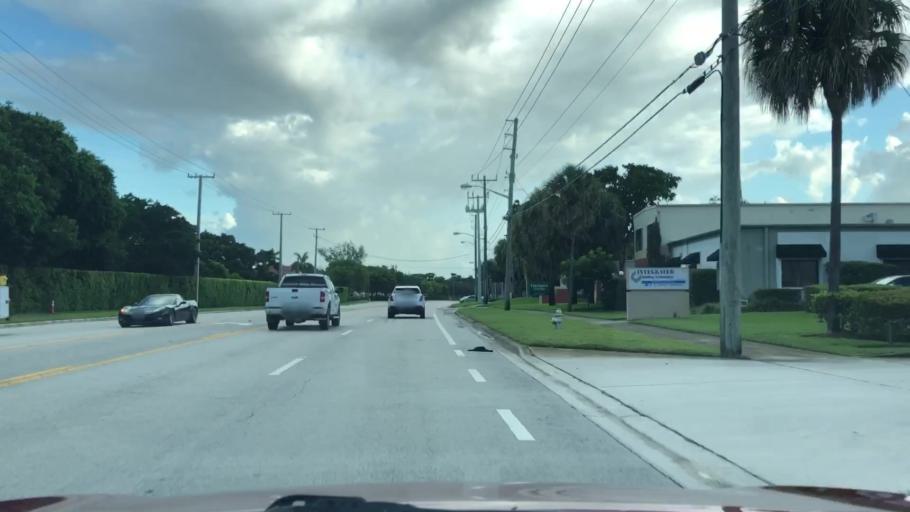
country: US
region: Florida
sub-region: Palm Beach County
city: Boca Raton
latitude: 26.3781
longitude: -80.0856
